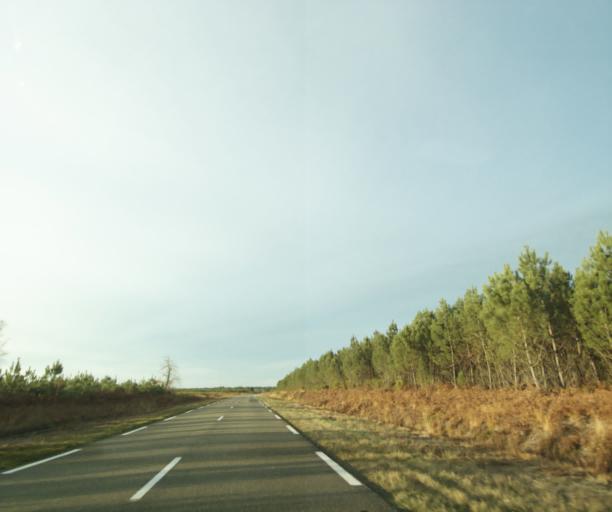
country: FR
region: Aquitaine
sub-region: Departement des Landes
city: Gabarret
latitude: 44.0777
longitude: -0.0689
